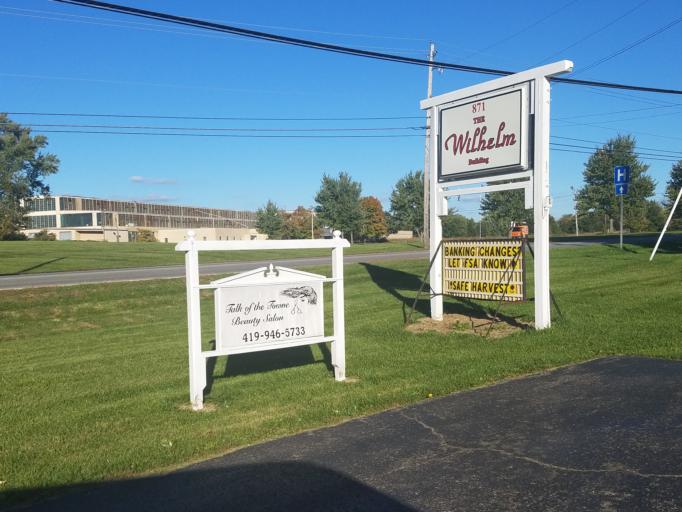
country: US
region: Ohio
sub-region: Morrow County
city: Mount Gilead
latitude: 40.5517
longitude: -82.8578
